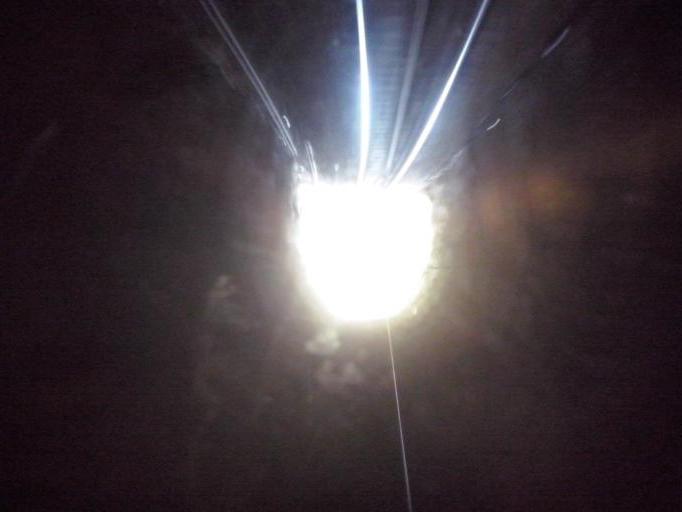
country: RS
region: Central Serbia
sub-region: Kolubarski Okrug
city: Valjevo
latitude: 44.2392
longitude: 19.8824
